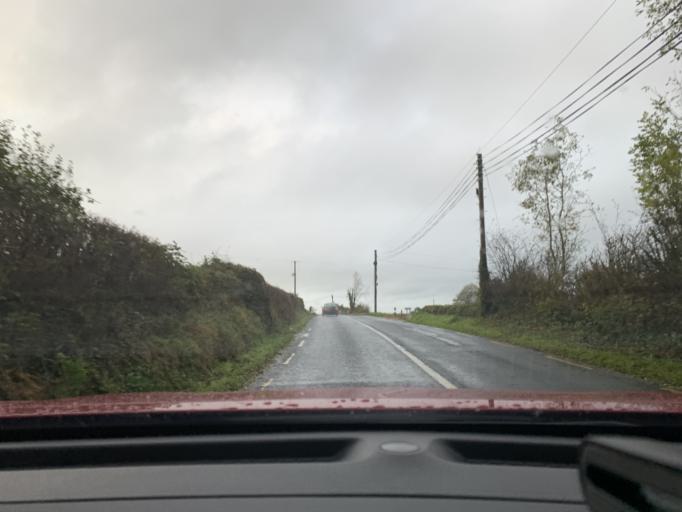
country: IE
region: Connaught
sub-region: Sligo
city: Ballymote
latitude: 54.0027
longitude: -8.5195
